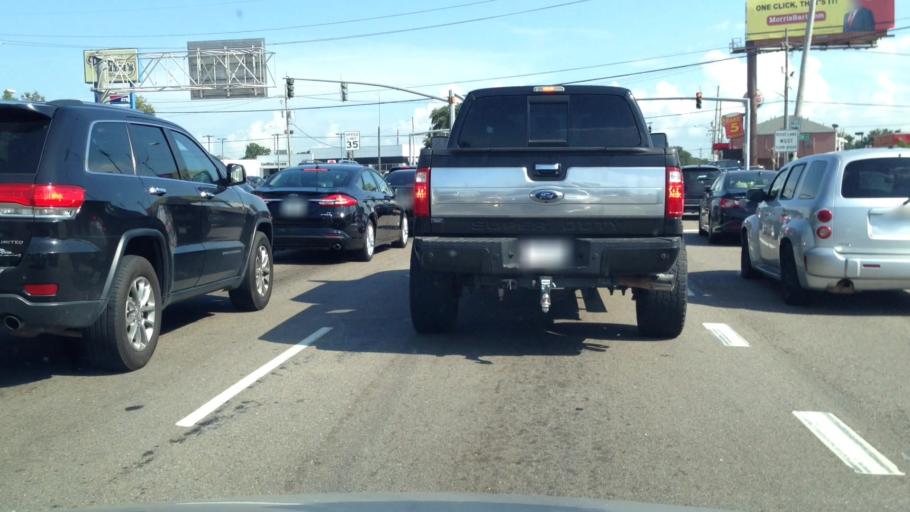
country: US
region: Louisiana
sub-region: Jefferson Parish
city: Metairie Terrace
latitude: 29.9946
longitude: -90.1820
